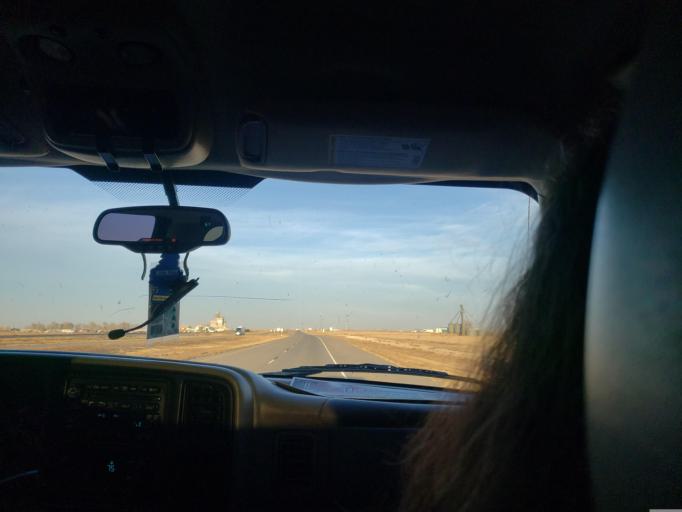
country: US
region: Oklahoma
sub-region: Texas County
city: Guymon
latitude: 36.7626
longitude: -101.3528
